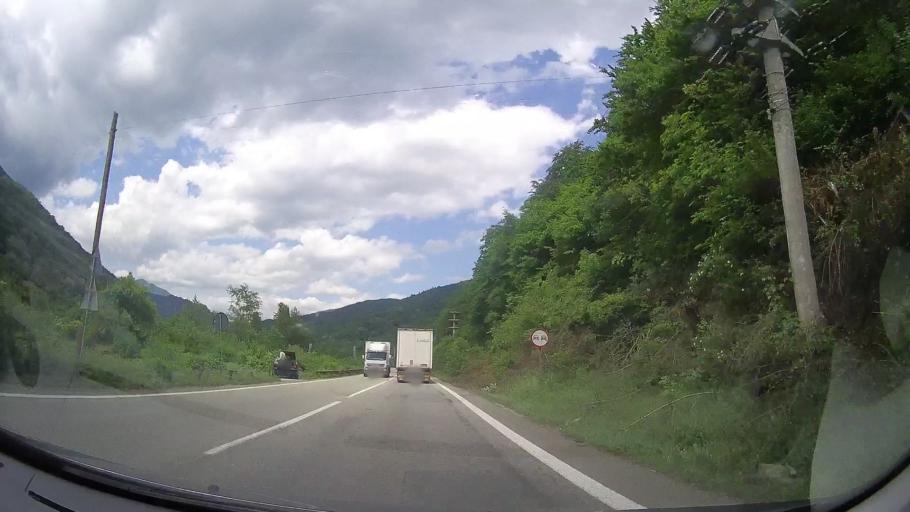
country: RO
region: Valcea
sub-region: Oras Calimanesti
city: Jiblea Veche
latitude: 45.2527
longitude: 24.3392
